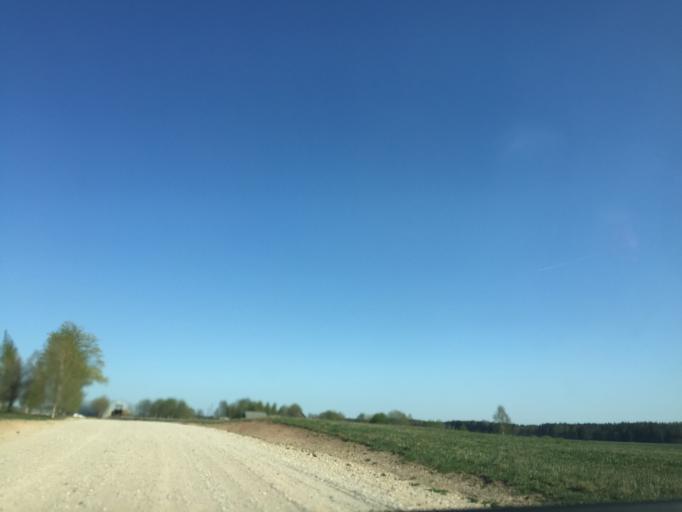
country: LV
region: Skriveri
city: Skriveri
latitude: 56.8329
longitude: 25.2202
